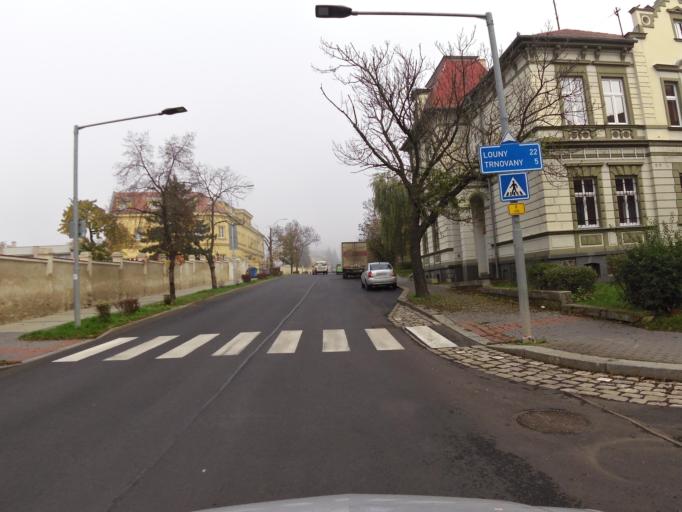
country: CZ
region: Ustecky
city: Zatec
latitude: 50.3246
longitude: 13.5484
